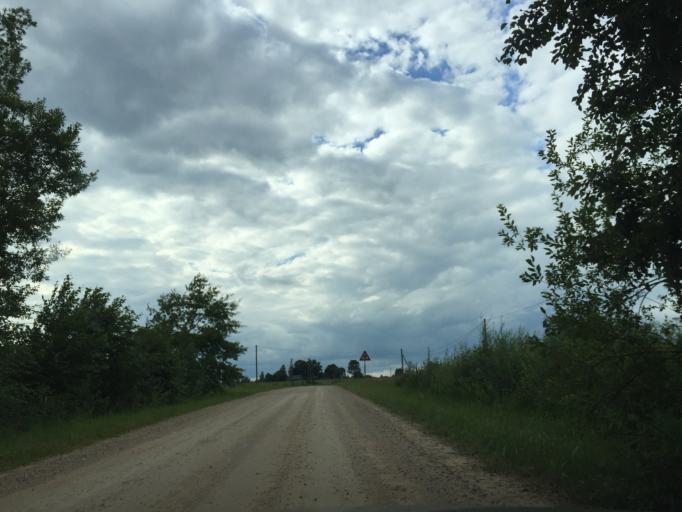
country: LV
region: Malpils
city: Malpils
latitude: 56.9651
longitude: 24.9795
